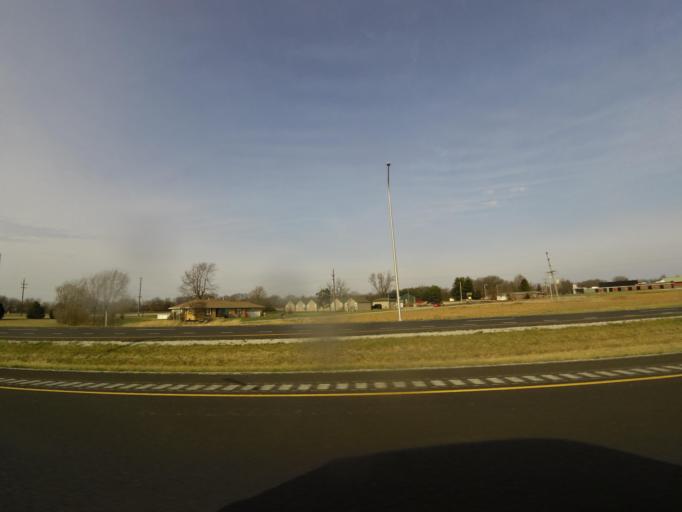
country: US
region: Illinois
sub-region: Macon County
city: Macon
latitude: 39.6990
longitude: -88.9973
